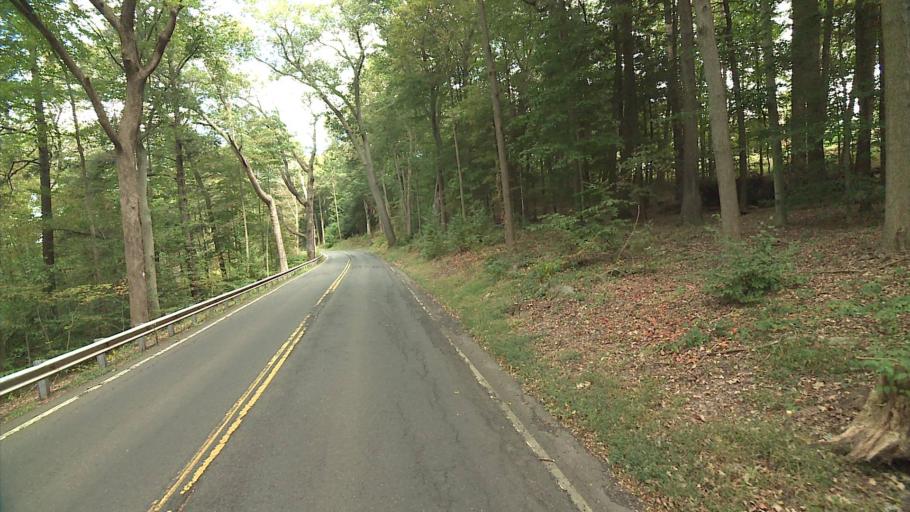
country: US
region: Connecticut
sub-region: Middlesex County
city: Middletown
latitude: 41.5394
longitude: -72.6829
